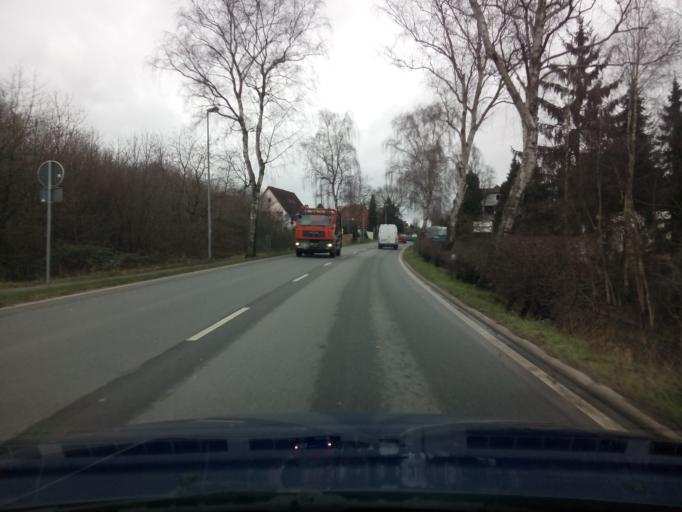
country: DE
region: Lower Saxony
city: Ritterhude
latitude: 53.1882
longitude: 8.7566
